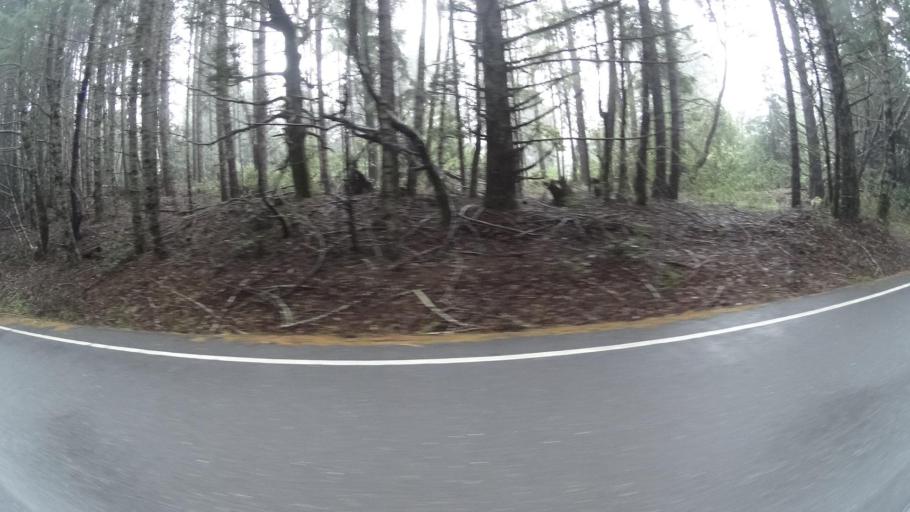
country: US
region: California
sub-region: Humboldt County
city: Westhaven-Moonstone
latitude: 41.2128
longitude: -123.9566
